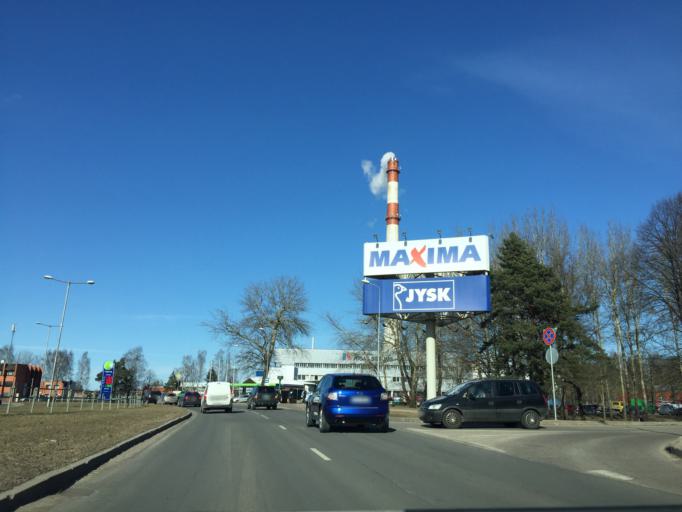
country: LV
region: Marupe
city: Marupe
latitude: 56.9601
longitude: 24.0353
